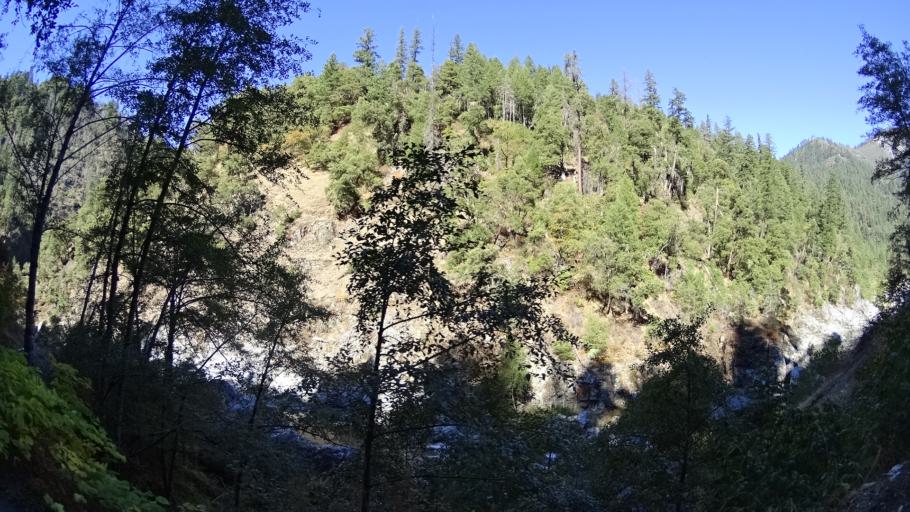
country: US
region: California
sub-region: Siskiyou County
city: Happy Camp
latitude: 41.3359
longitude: -123.3925
